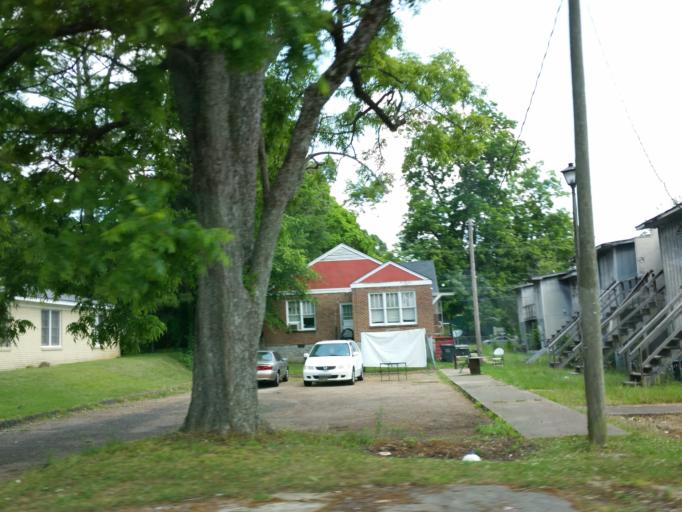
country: US
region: Mississippi
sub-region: Lauderdale County
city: Meridian
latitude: 32.3774
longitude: -88.7199
